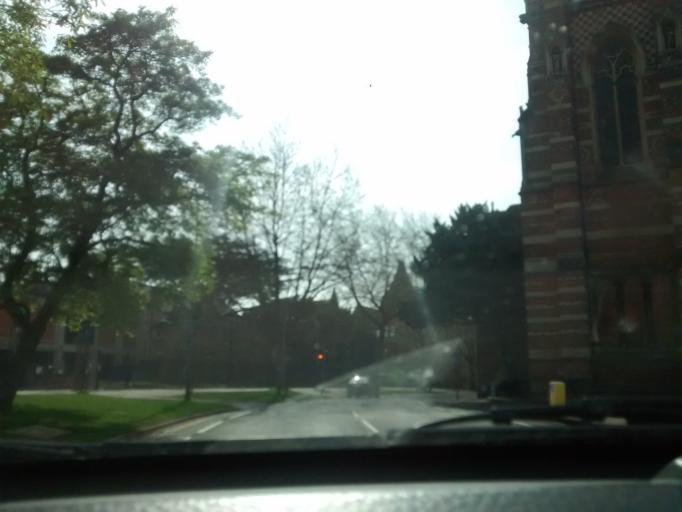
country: GB
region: England
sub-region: Oxfordshire
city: Oxford
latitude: 51.7598
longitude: -1.2577
